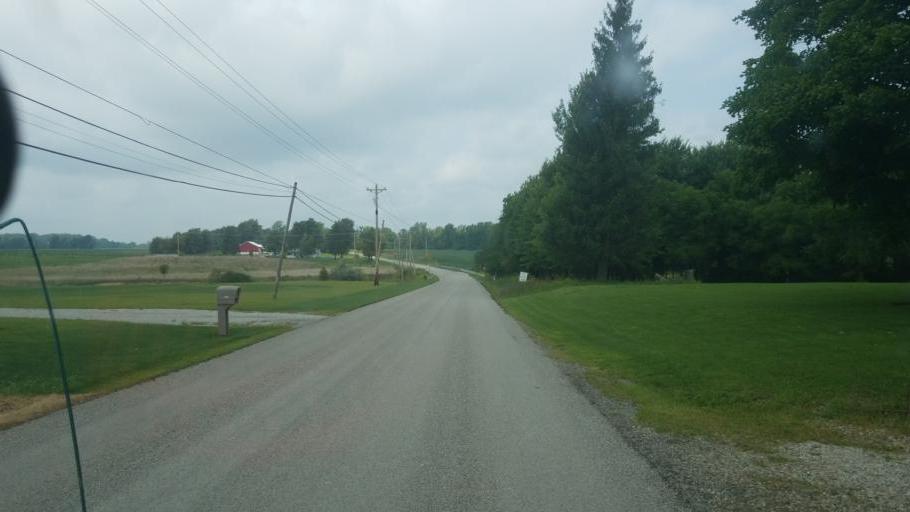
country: US
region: Ohio
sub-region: Huron County
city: Greenwich
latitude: 41.0499
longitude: -82.5187
